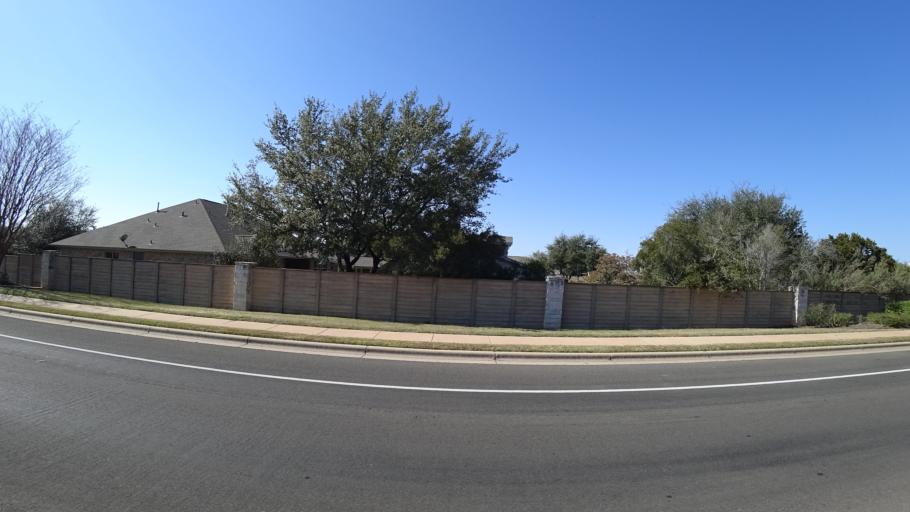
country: US
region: Texas
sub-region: Williamson County
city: Anderson Mill
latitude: 30.3847
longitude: -97.8509
